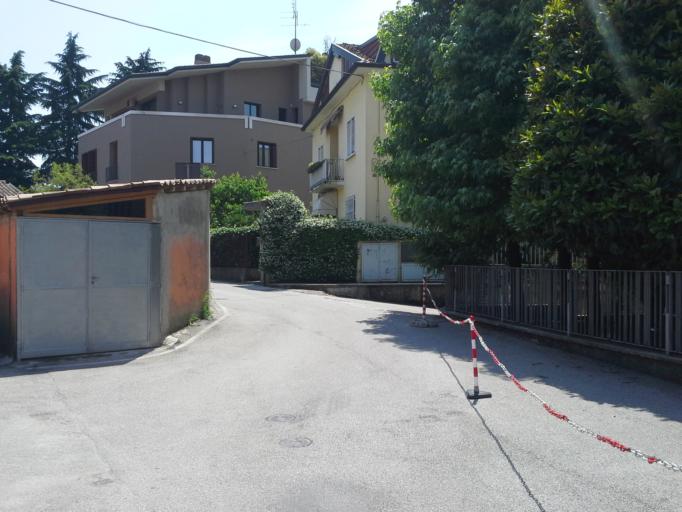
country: IT
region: Lombardy
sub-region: Provincia di Brescia
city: Desenzano del Garda
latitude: 45.4681
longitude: 10.5397
